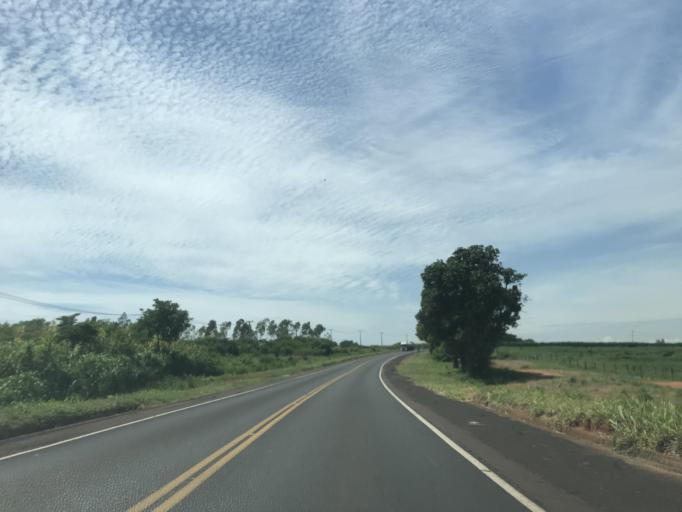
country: BR
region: Parana
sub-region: Paranavai
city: Nova Aurora
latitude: -22.9748
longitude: -52.6084
